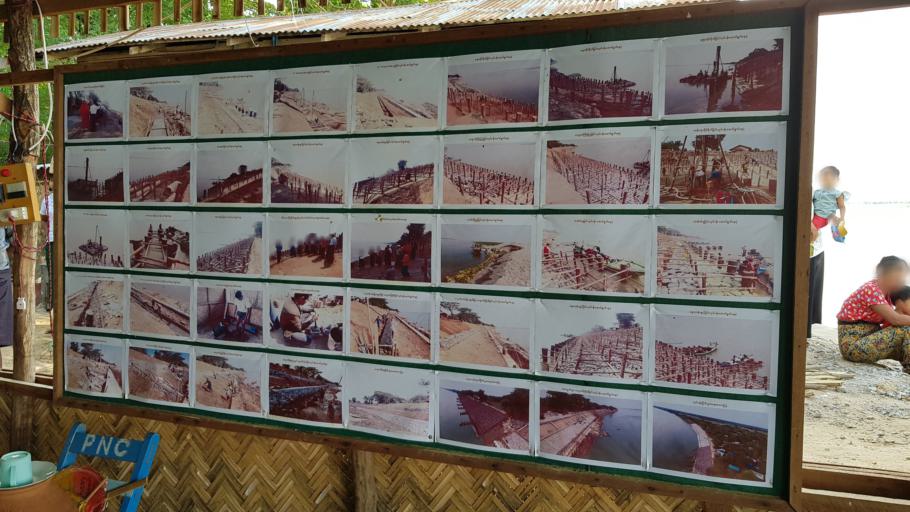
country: MM
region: Sagain
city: Sagaing
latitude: 21.8650
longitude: 95.8989
